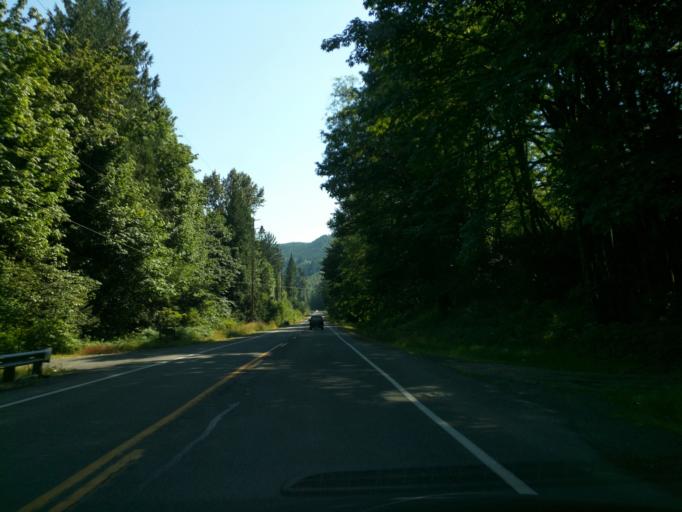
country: US
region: Washington
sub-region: Whatcom County
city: Peaceful Valley
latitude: 48.8879
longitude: -122.1527
